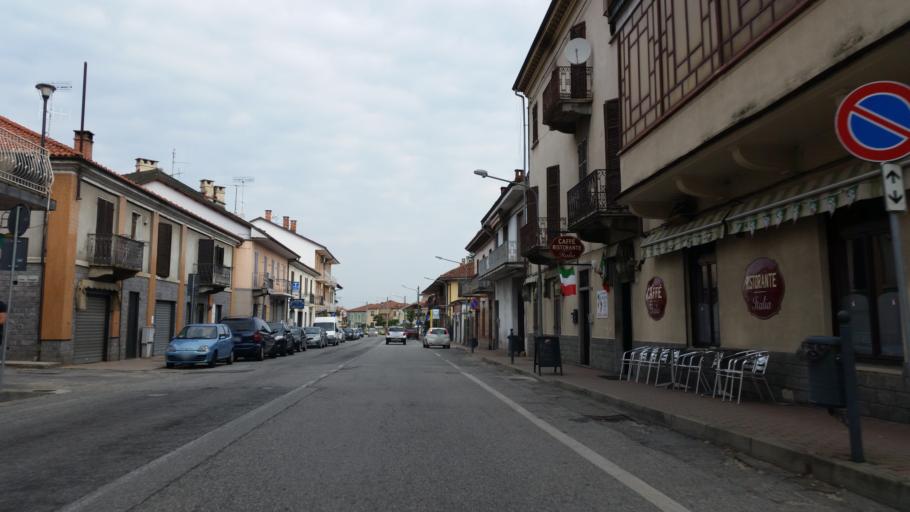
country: IT
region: Piedmont
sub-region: Provincia di Torino
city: Cavagnolo
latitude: 45.1533
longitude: 8.0509
